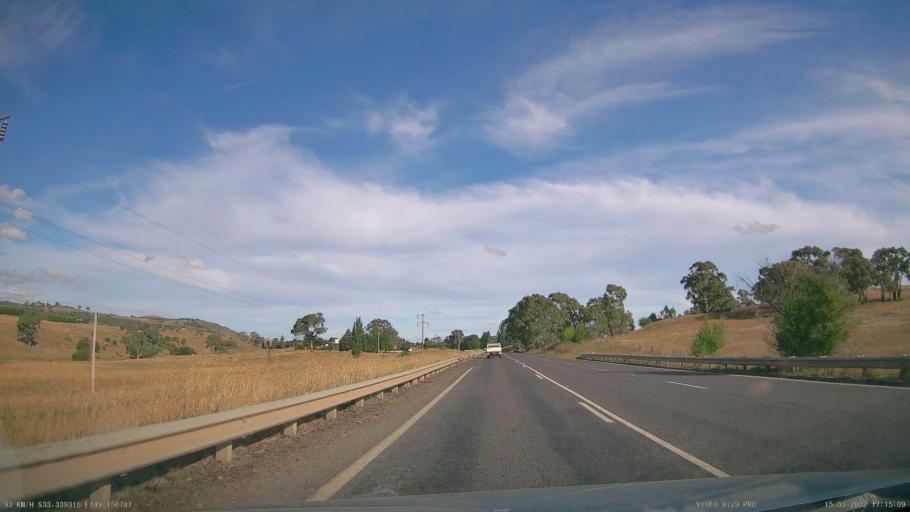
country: AU
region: New South Wales
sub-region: Orange Municipality
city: Orange
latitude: -33.3395
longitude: 149.1569
